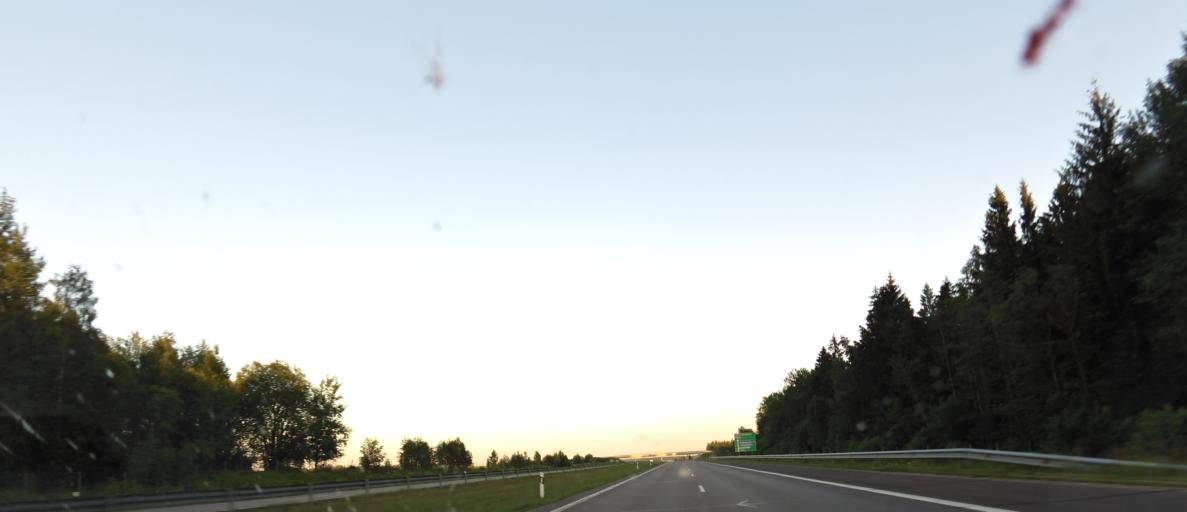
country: LT
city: Sirvintos
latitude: 54.9518
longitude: 24.9625
